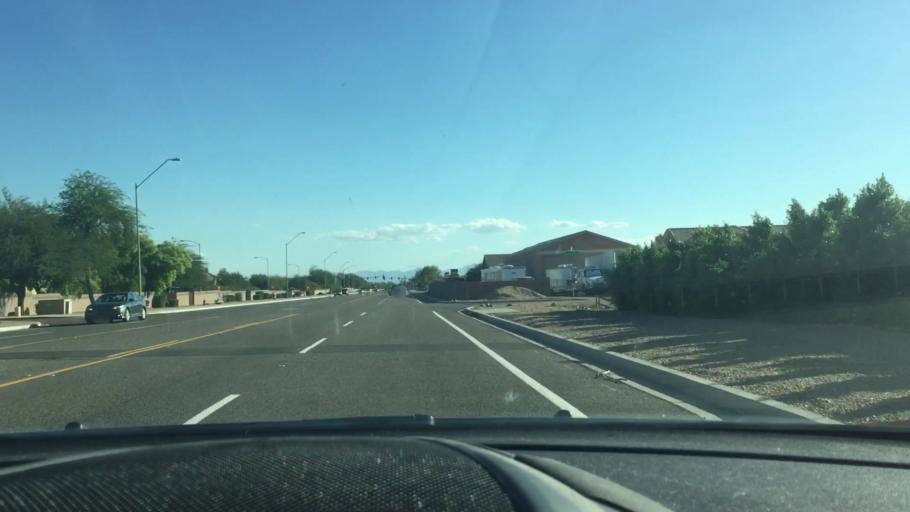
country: US
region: Arizona
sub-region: Maricopa County
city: Sun City
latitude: 33.7003
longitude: -112.2377
